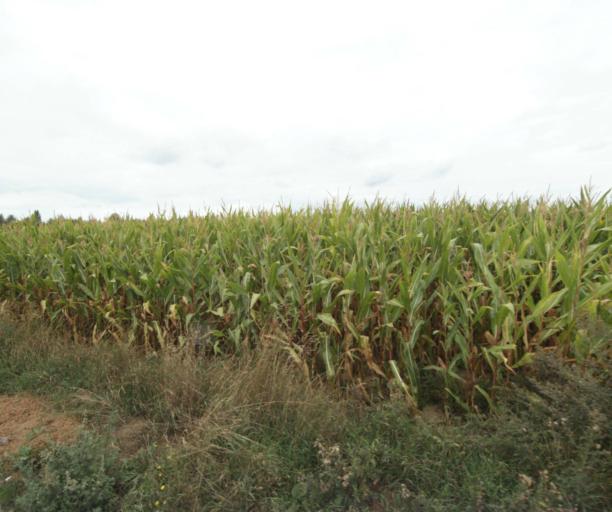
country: FR
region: Nord-Pas-de-Calais
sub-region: Departement du Nord
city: Fretin
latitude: 50.5598
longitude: 3.1299
